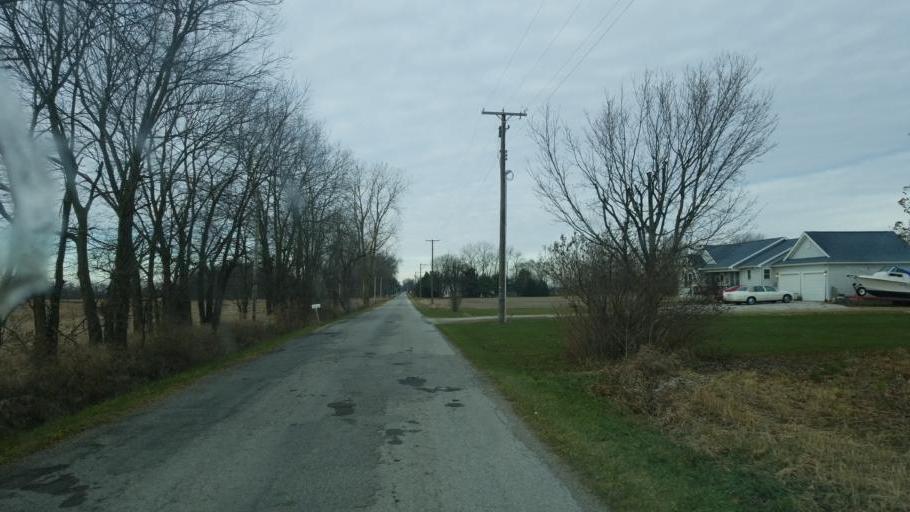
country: US
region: Ohio
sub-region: Morrow County
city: Mount Gilead
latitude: 40.6306
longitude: -82.8760
